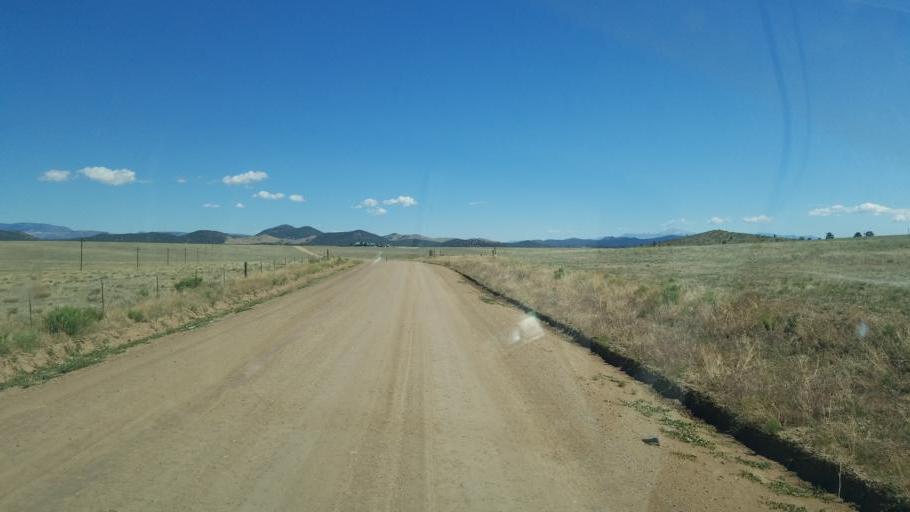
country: US
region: Colorado
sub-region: Custer County
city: Westcliffe
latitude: 38.2497
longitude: -105.5001
